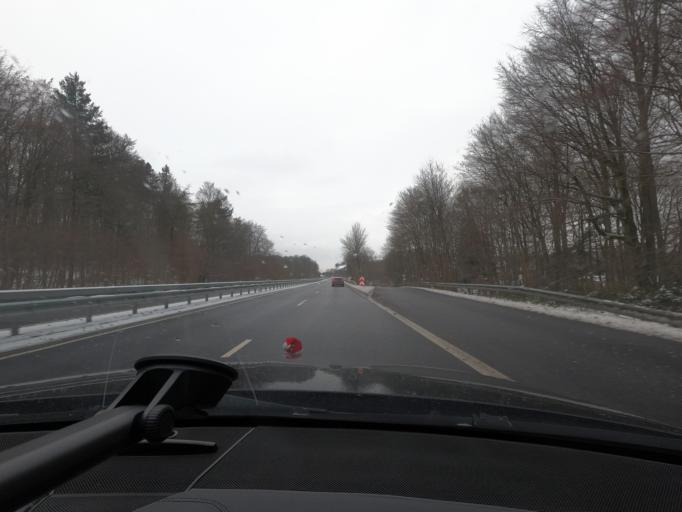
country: DK
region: South Denmark
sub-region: Aabenraa Kommune
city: Krusa
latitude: 54.8289
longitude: 9.4143
